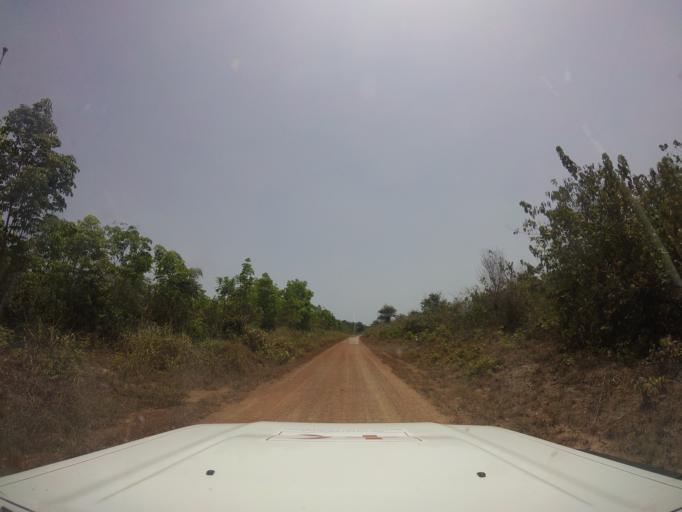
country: LR
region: Grand Cape Mount
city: Robertsport
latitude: 6.9338
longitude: -11.3413
